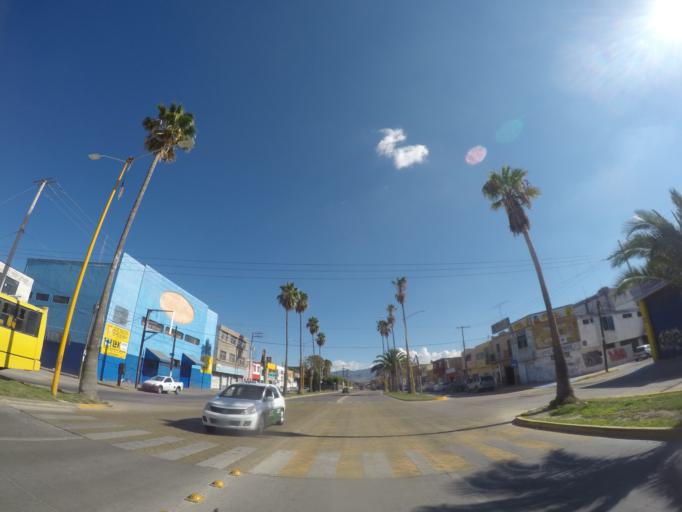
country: MX
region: San Luis Potosi
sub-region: San Luis Potosi
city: San Luis Potosi
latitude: 22.1626
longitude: -100.9719
